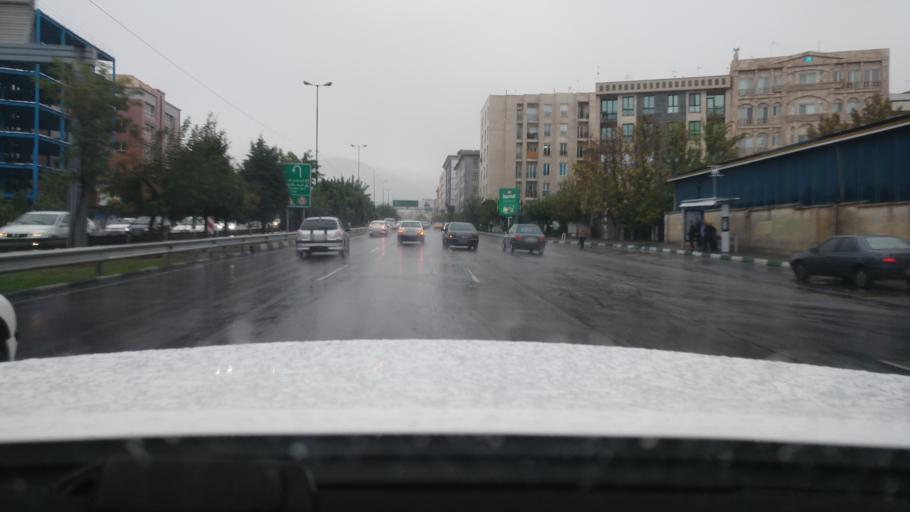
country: IR
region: Tehran
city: Tehran
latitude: 35.7262
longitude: 51.3098
